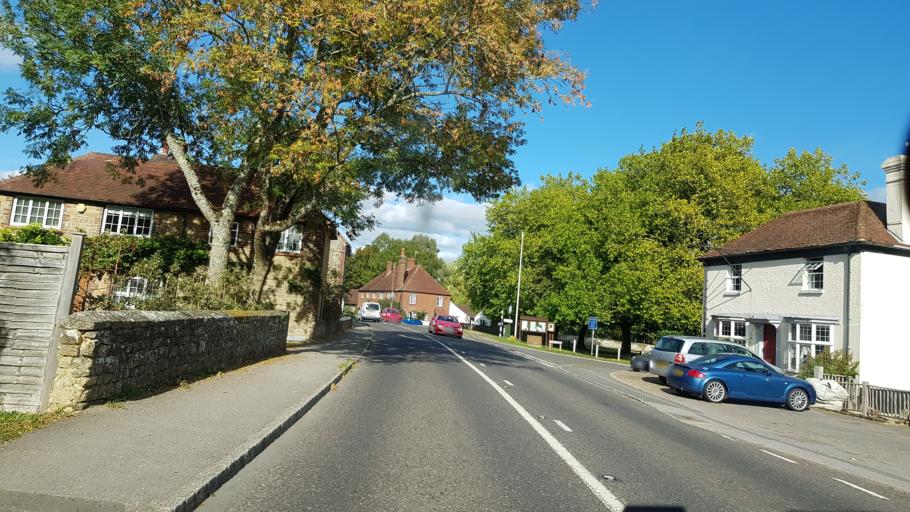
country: GB
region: England
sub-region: Surrey
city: Chiddingfold
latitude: 51.0567
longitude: -0.6432
